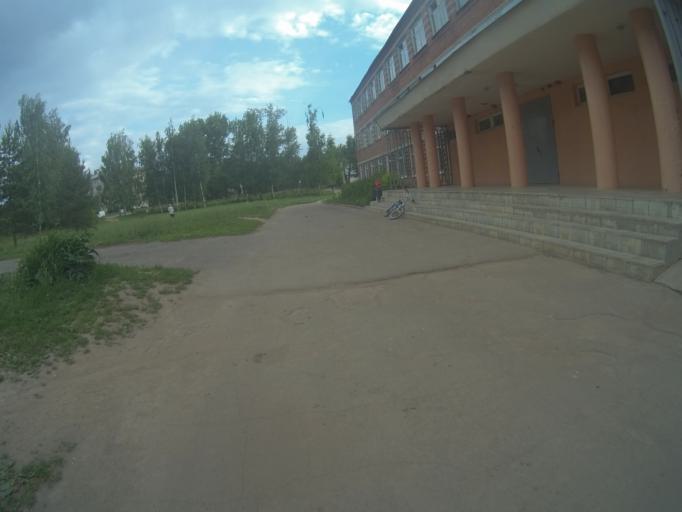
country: RU
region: Vladimir
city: Vladimir
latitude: 56.2219
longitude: 40.4075
